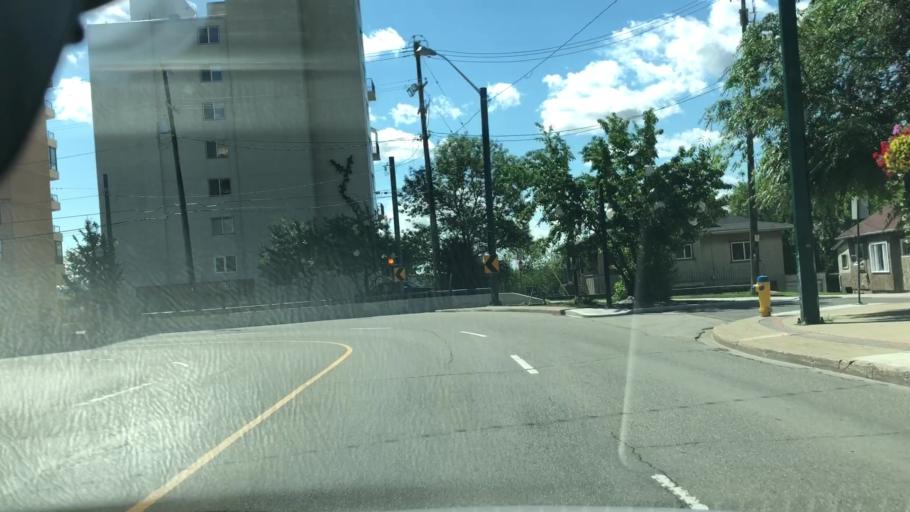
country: CA
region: Alberta
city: Edmonton
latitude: 53.5417
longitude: -113.5359
